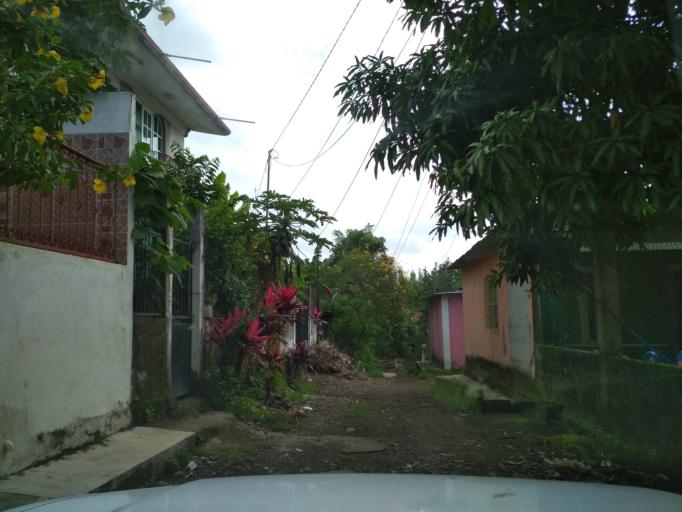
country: MX
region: Veracruz
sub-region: San Andres Tuxtla
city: Matacapan
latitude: 18.4410
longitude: -95.1772
